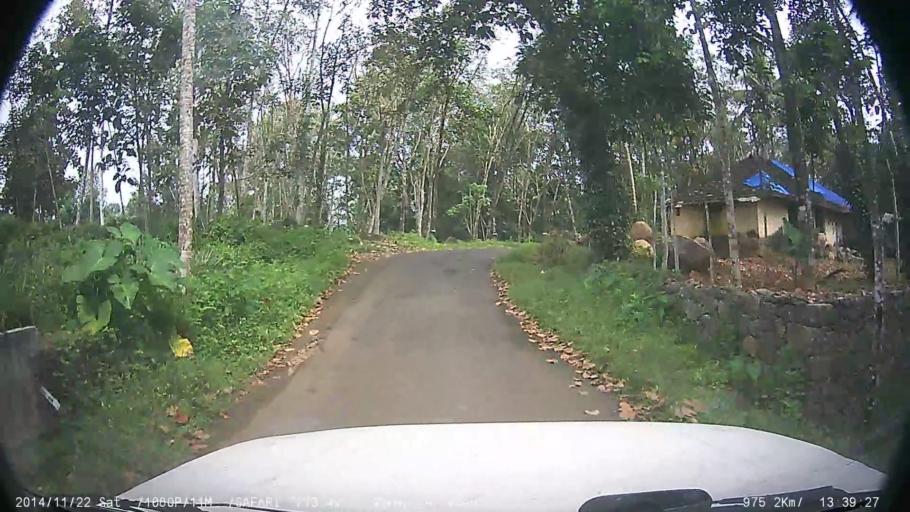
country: IN
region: Kerala
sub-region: Kottayam
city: Palackattumala
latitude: 9.7866
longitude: 76.5551
